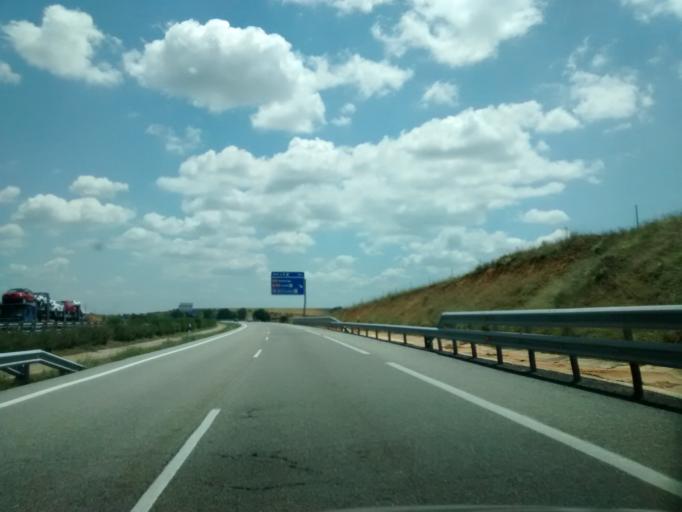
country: ES
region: Castille and Leon
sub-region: Provincia de Leon
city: Astorga
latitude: 42.4416
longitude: -6.0704
